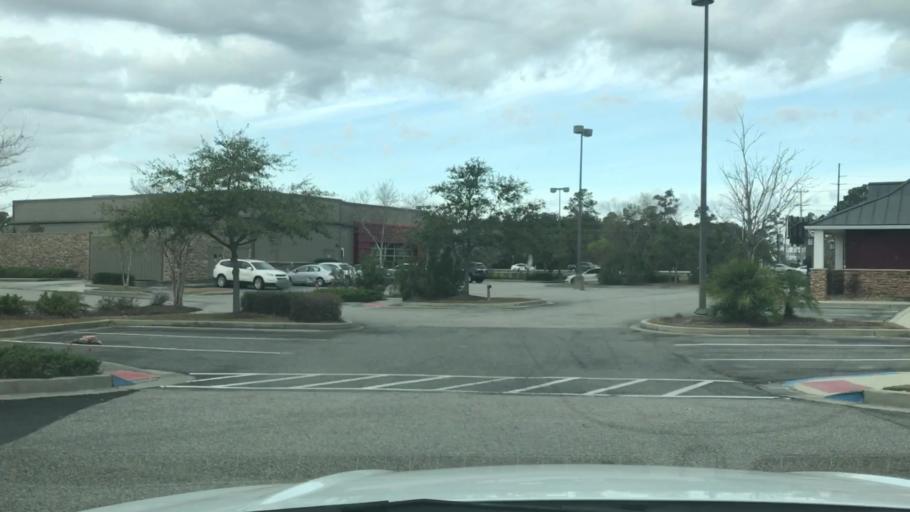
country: US
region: South Carolina
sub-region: Horry County
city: Myrtle Beach
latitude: 33.7055
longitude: -78.9204
